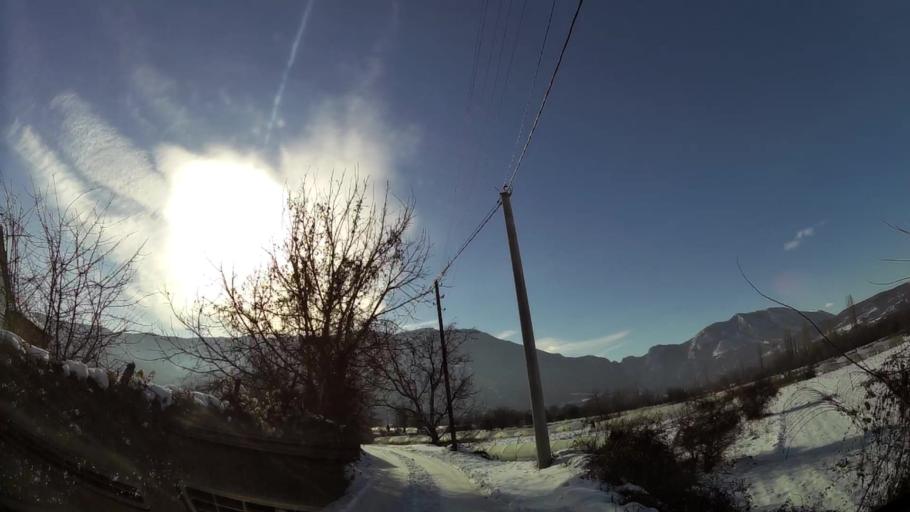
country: MK
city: Grchec
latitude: 41.9892
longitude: 21.3257
